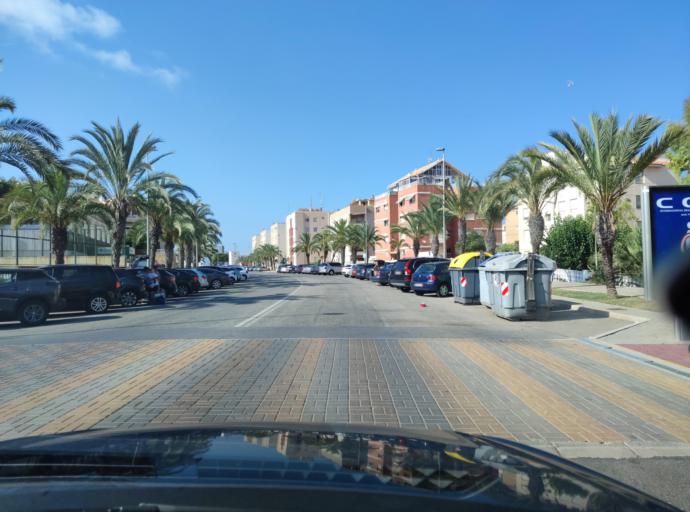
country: ES
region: Valencia
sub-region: Provincia de Alicante
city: Guardamar del Segura
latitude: 38.0757
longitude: -0.6504
